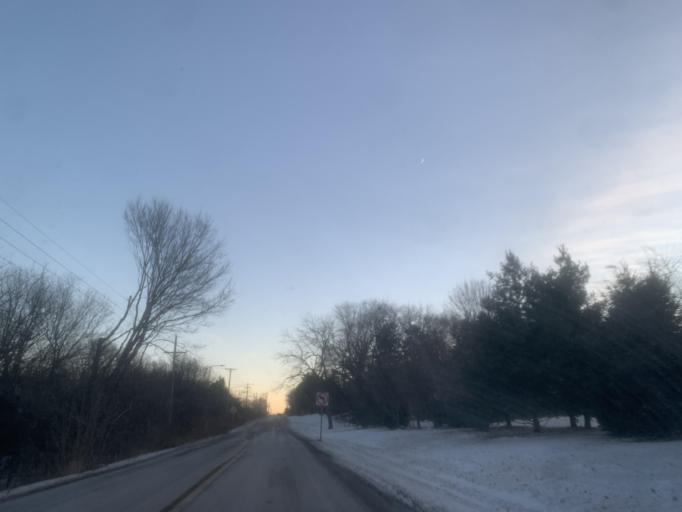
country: US
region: Nebraska
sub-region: Douglas County
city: Ralston
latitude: 41.2667
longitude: -96.0622
